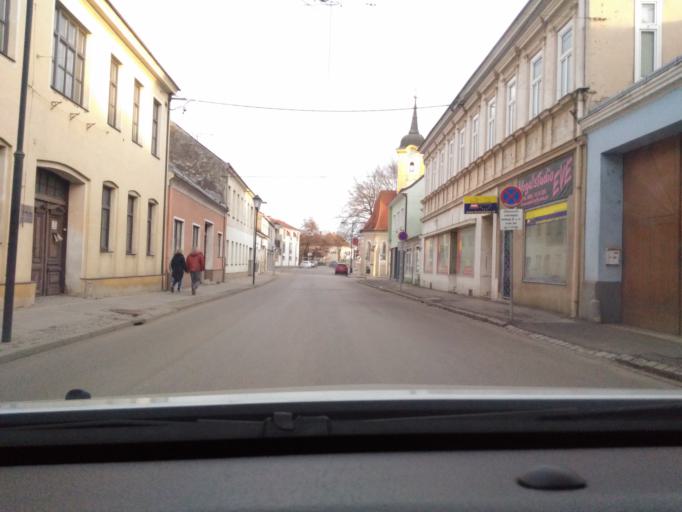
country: AT
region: Lower Austria
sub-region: Politischer Bezirk Mistelbach
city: Laa an der Thaya
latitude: 48.7204
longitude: 16.3864
